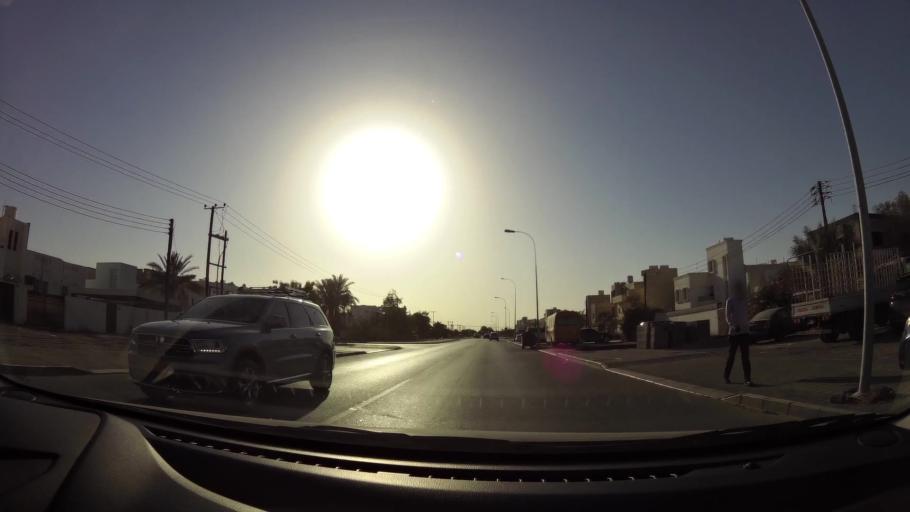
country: OM
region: Muhafazat Masqat
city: As Sib al Jadidah
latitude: 23.6307
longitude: 58.1949
